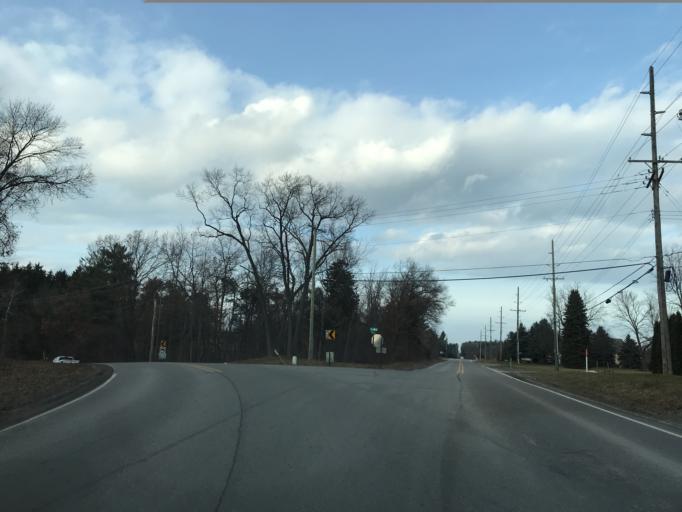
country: US
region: Michigan
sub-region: Oakland County
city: South Lyon
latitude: 42.4657
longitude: -83.6968
